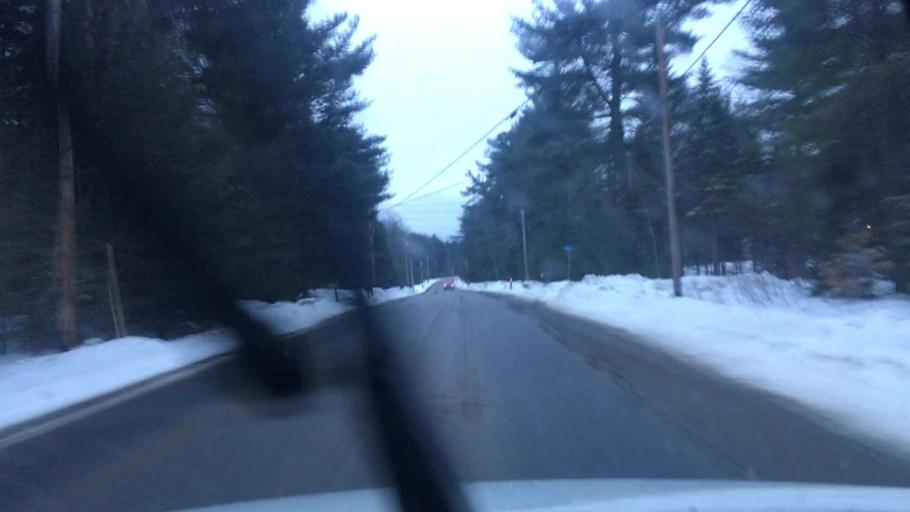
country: US
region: Maine
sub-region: Kennebec County
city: Oakland
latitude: 44.6238
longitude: -69.7268
